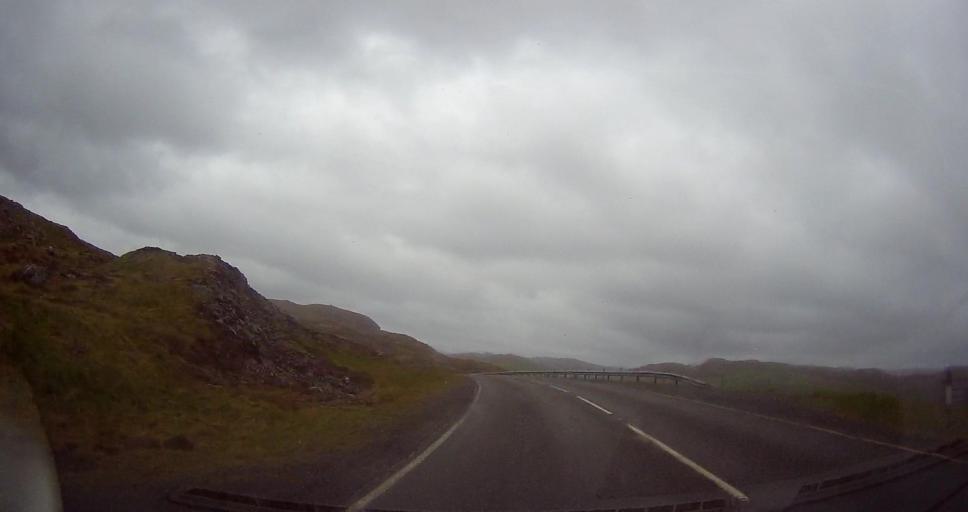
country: GB
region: Scotland
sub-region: Shetland Islands
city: Lerwick
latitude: 60.4191
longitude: -1.3939
